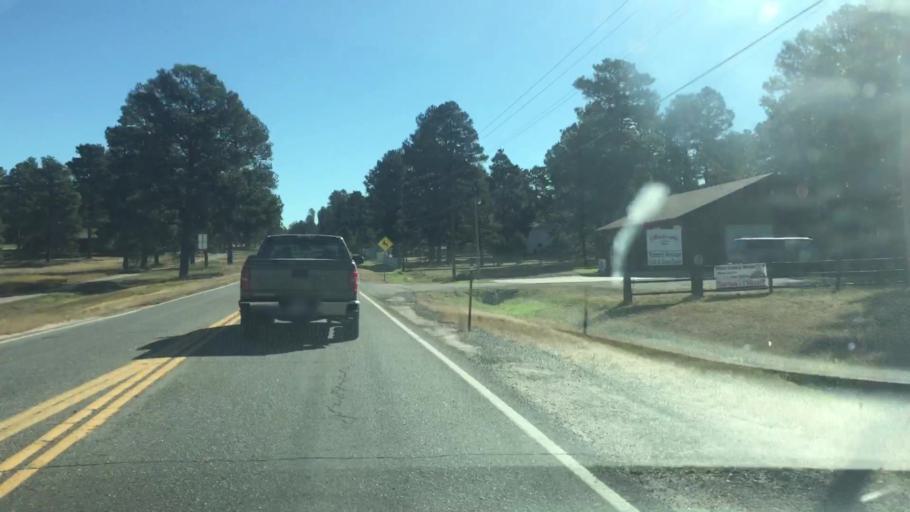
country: US
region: Colorado
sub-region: Elbert County
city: Elizabeth
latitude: 39.3614
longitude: -104.5885
